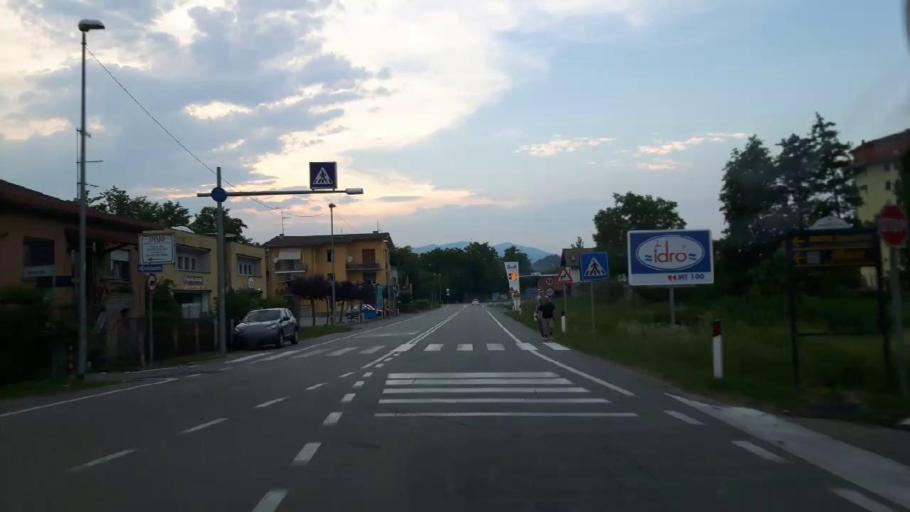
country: IT
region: Piedmont
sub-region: Provincia di Novara
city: Dormelletto
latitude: 45.7443
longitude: 8.5662
